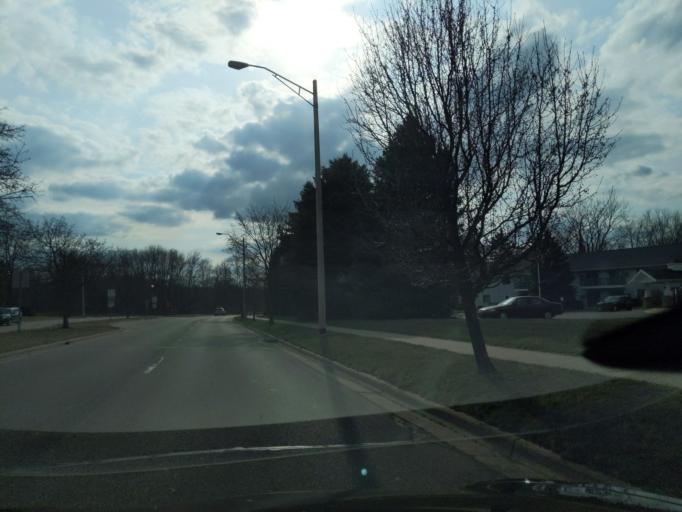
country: US
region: Michigan
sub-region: Ingham County
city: Holt
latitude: 42.6611
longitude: -84.5540
